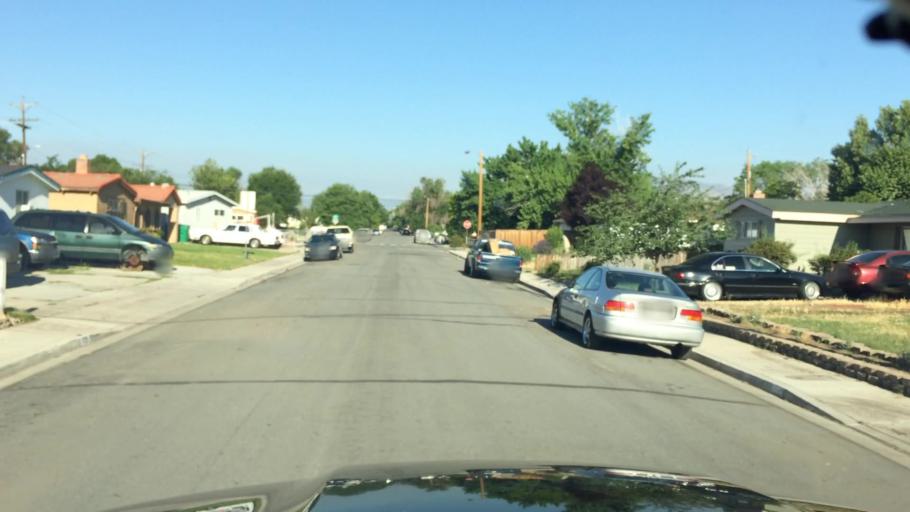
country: US
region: Nevada
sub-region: Washoe County
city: Sparks
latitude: 39.5460
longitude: -119.7579
